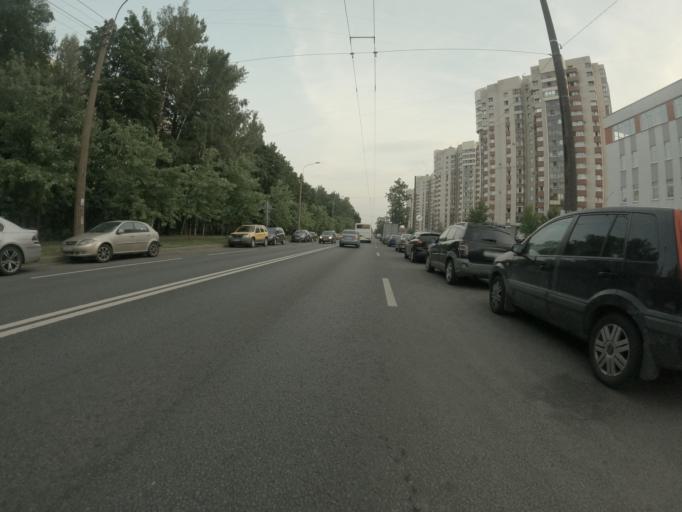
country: RU
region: Leningrad
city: Kalininskiy
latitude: 59.9824
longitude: 30.3973
